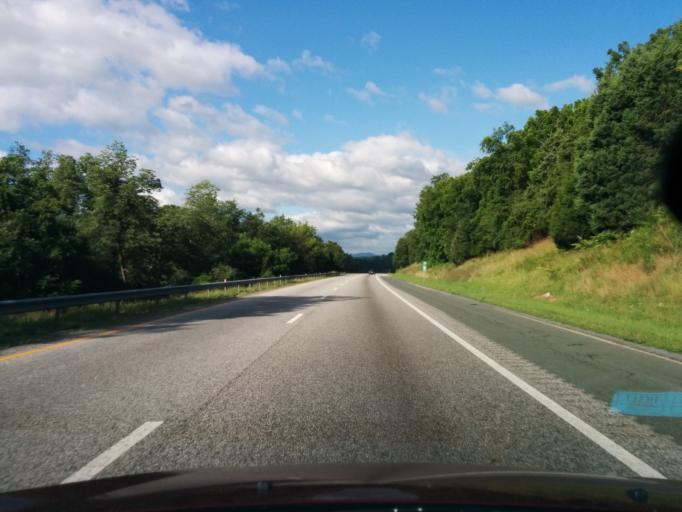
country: US
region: Virginia
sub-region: City of Lexington
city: Lexington
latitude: 37.7143
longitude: -79.4492
